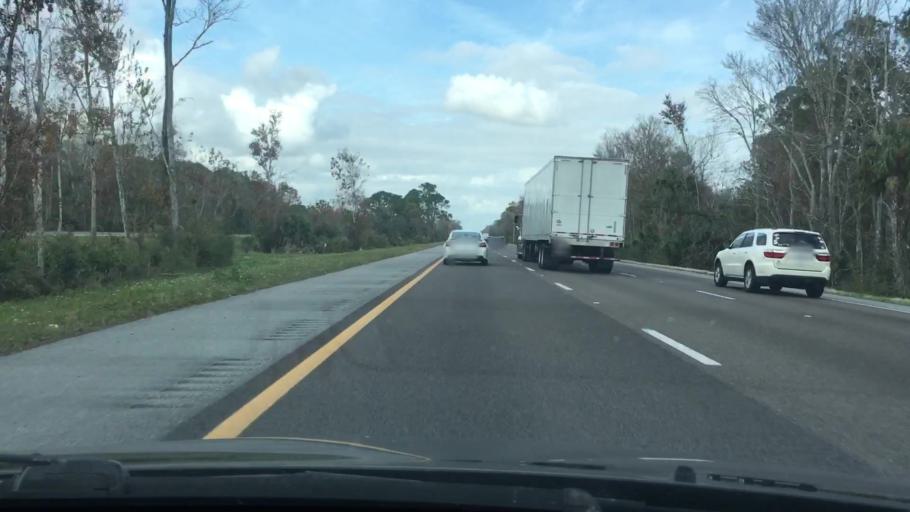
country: US
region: Florida
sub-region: Volusia County
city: Oak Hill
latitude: 28.9049
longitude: -80.9325
